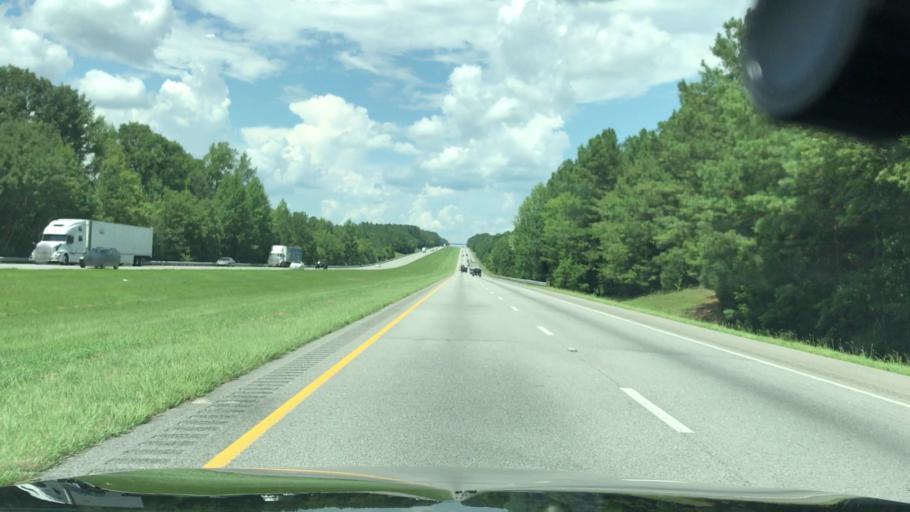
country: US
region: South Carolina
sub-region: Chester County
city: Great Falls
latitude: 34.6600
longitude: -81.0288
